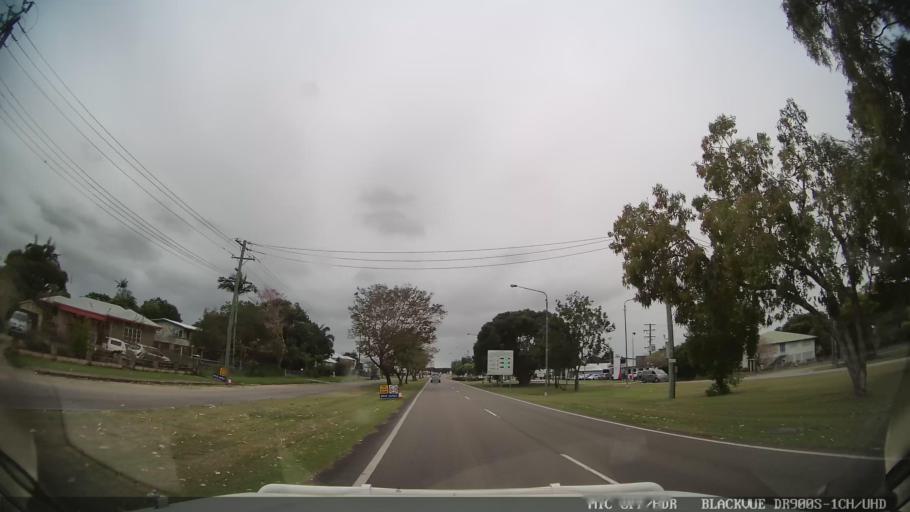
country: AU
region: Queensland
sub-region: Hinchinbrook
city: Ingham
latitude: -18.6454
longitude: 146.1622
